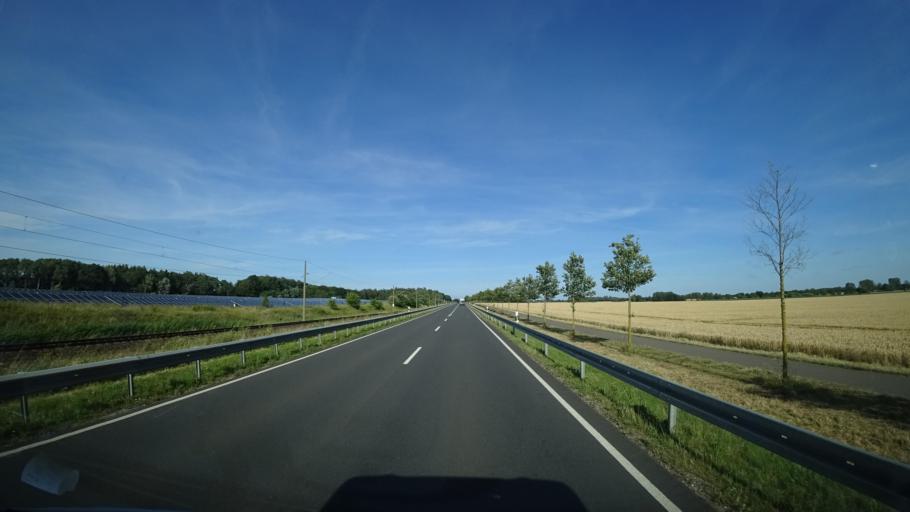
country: DE
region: Mecklenburg-Vorpommern
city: Niepars
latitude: 54.2988
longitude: 12.8952
